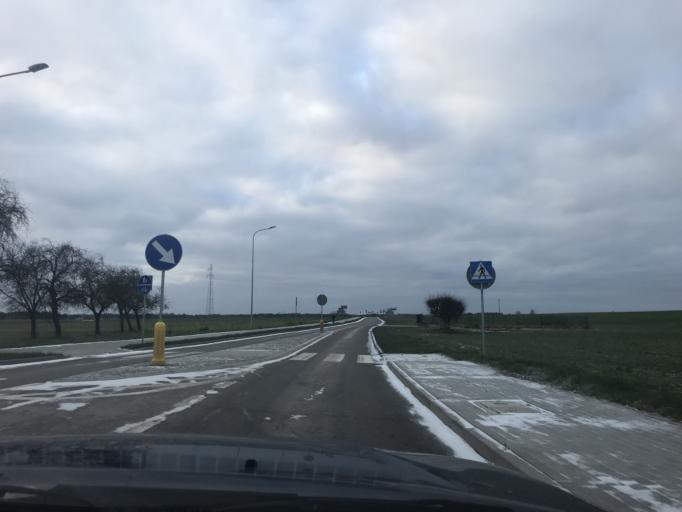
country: PL
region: Pomeranian Voivodeship
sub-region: Powiat chojnicki
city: Brusy
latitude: 53.8734
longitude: 17.7535
